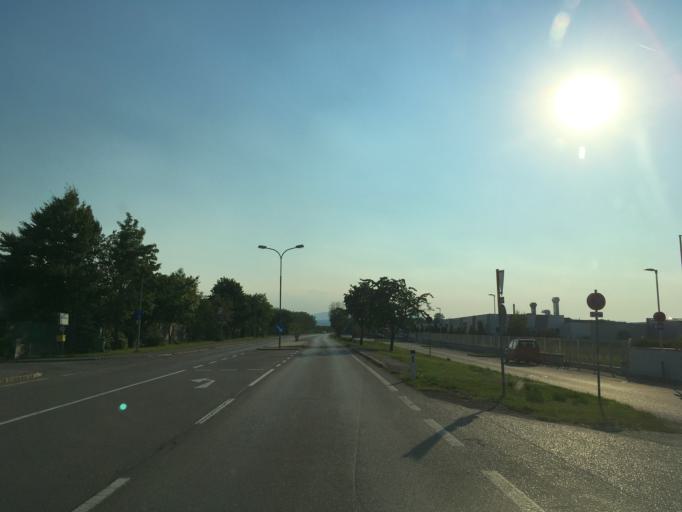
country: AT
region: Lower Austria
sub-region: Politischer Bezirk Baden
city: Schonau an der Triesting
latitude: 47.9427
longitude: 16.2520
